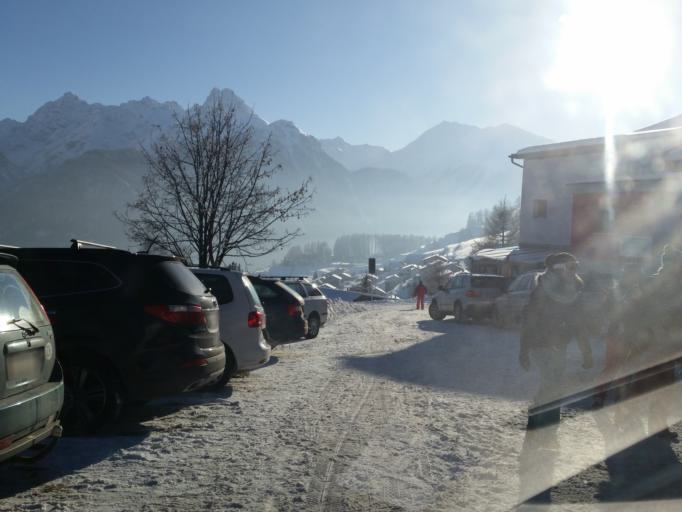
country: CH
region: Grisons
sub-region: Inn District
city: Scuol
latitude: 46.7951
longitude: 10.2463
